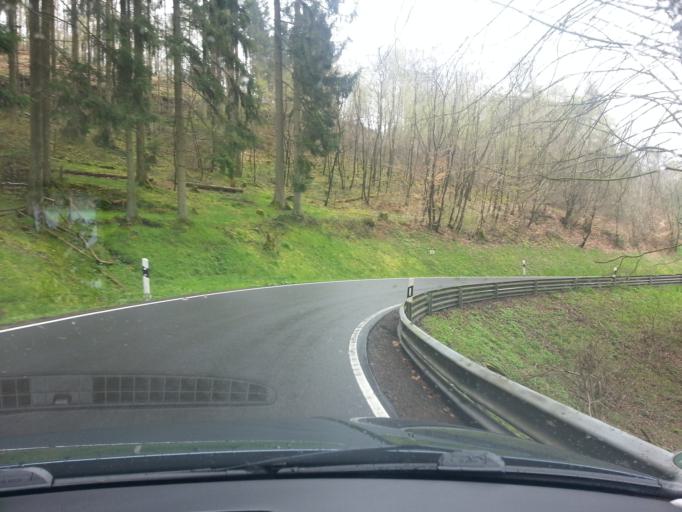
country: DE
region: Rheinland-Pfalz
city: Kashofen
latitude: 49.3193
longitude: 7.3910
